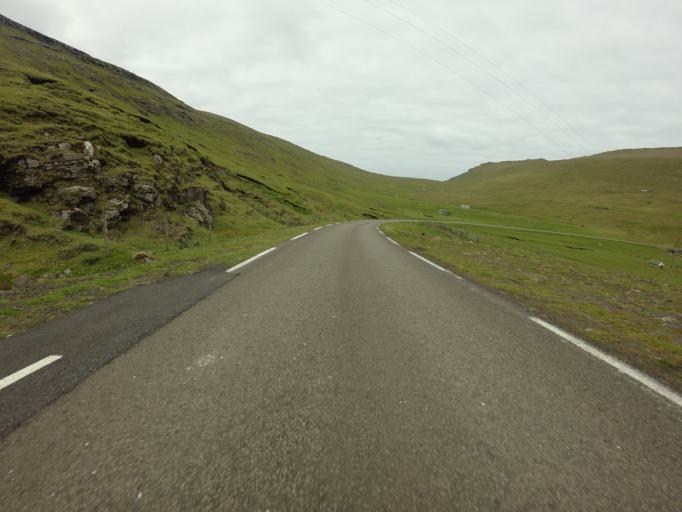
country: FO
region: Suduroy
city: Tvoroyri
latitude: 61.6251
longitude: -6.9414
